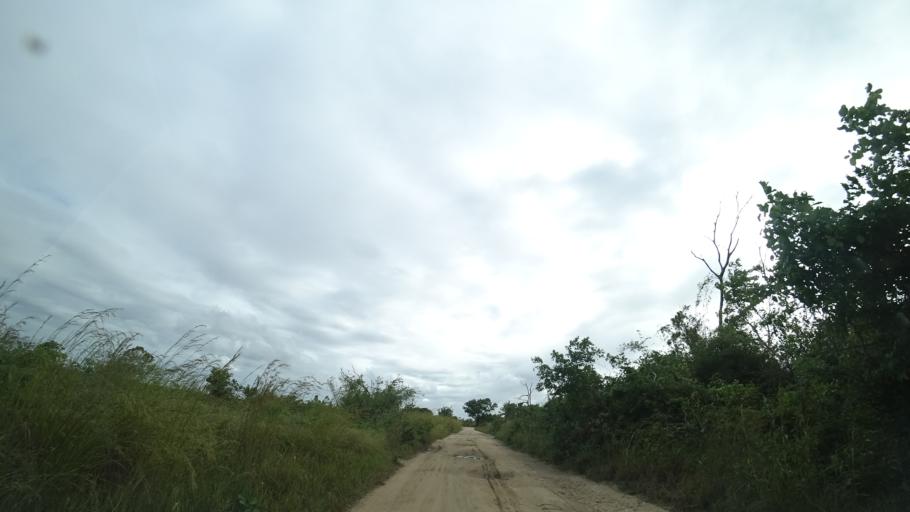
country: MZ
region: Sofala
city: Dondo
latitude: -19.5753
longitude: 35.0895
